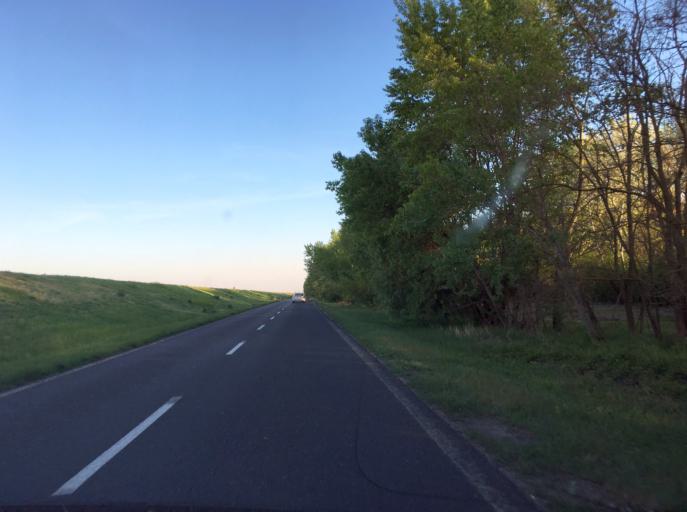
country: HU
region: Gyor-Moson-Sopron
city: Rajka
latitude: 48.0245
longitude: 17.2447
